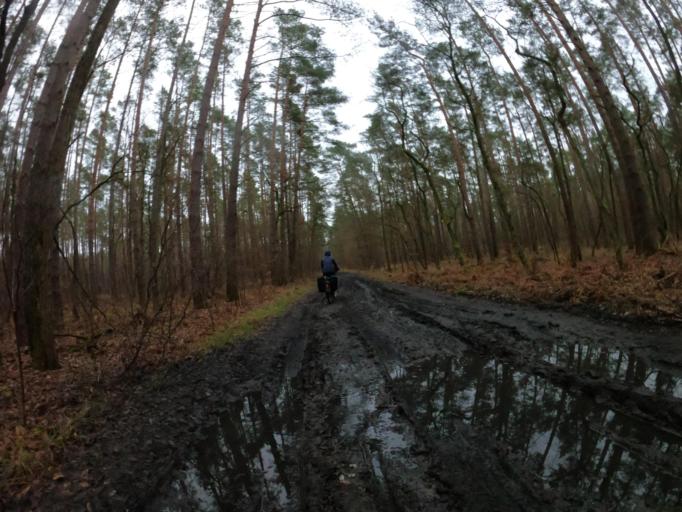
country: PL
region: West Pomeranian Voivodeship
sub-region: Powiat mysliborski
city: Debno
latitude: 52.7101
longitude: 14.7150
